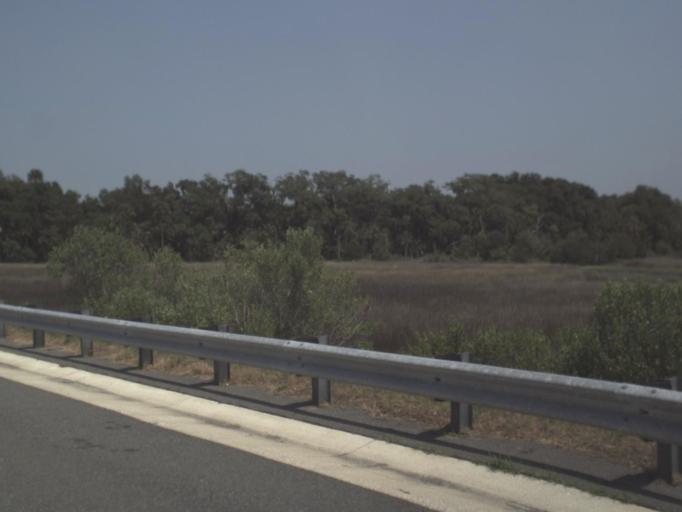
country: US
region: Florida
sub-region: Duval County
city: Atlantic Beach
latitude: 30.3649
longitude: -81.4313
